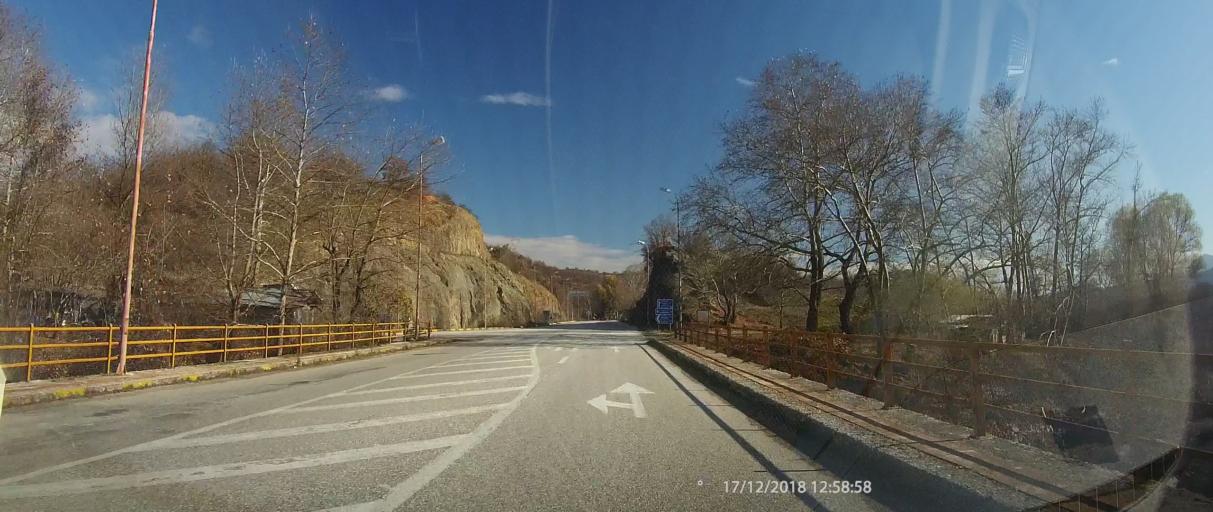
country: GR
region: Thessaly
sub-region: Trikala
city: Kastraki
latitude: 39.7386
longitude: 21.5498
